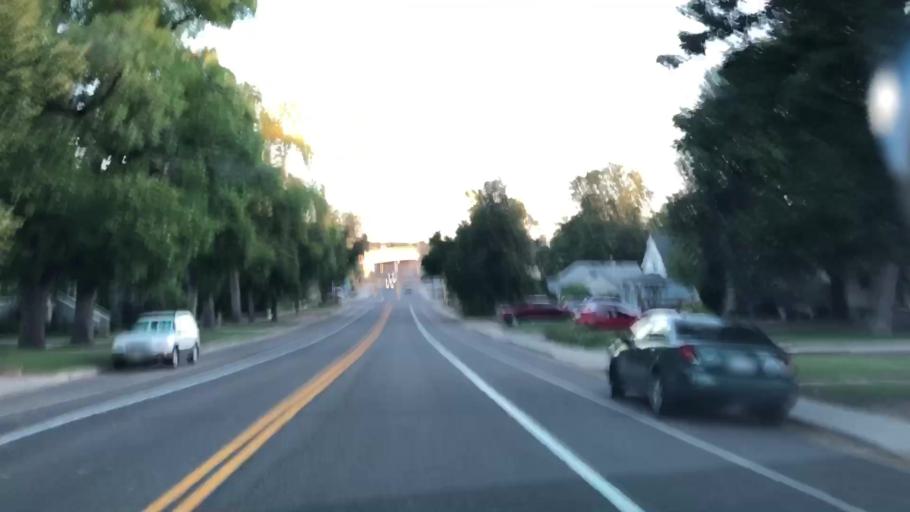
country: US
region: Colorado
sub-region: Boulder County
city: Longmont
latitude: 40.1633
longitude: -105.1069
